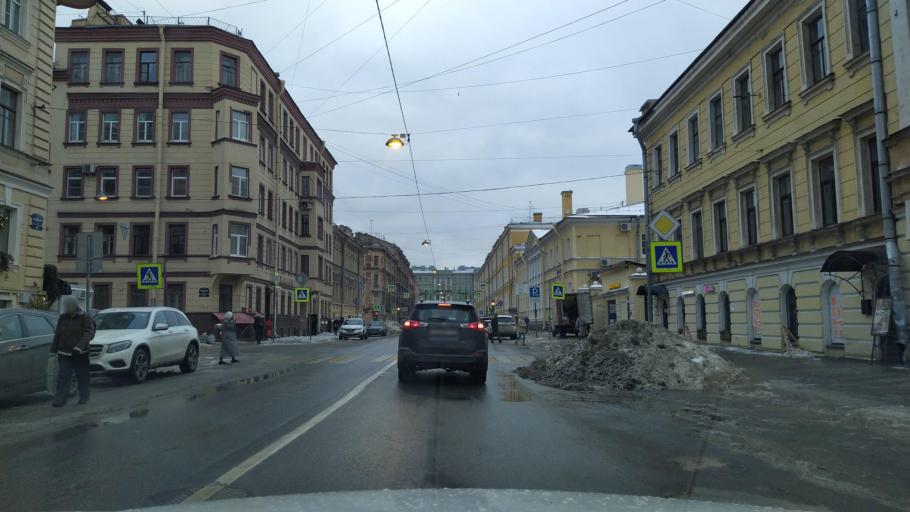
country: RU
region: St.-Petersburg
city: Centralniy
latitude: 59.9414
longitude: 30.3637
